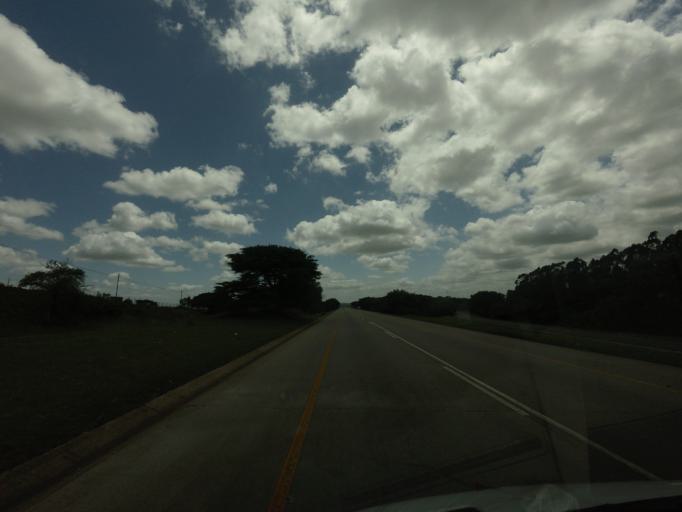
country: ZA
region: KwaZulu-Natal
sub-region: uMkhanyakude District Municipality
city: Mtubatuba
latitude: -28.4734
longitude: 32.1453
